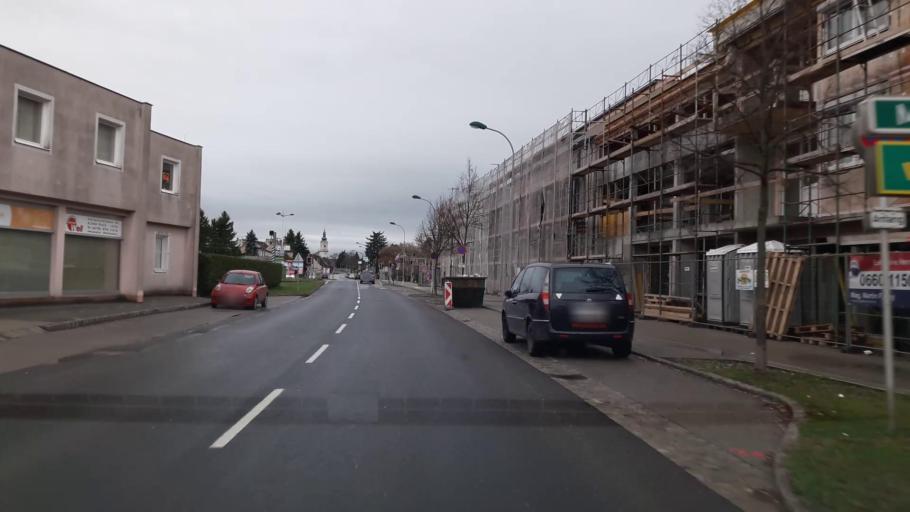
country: AT
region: Burgenland
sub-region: Politischer Bezirk Neusiedl am See
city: Bruckneudorf
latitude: 48.0326
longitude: 16.7832
